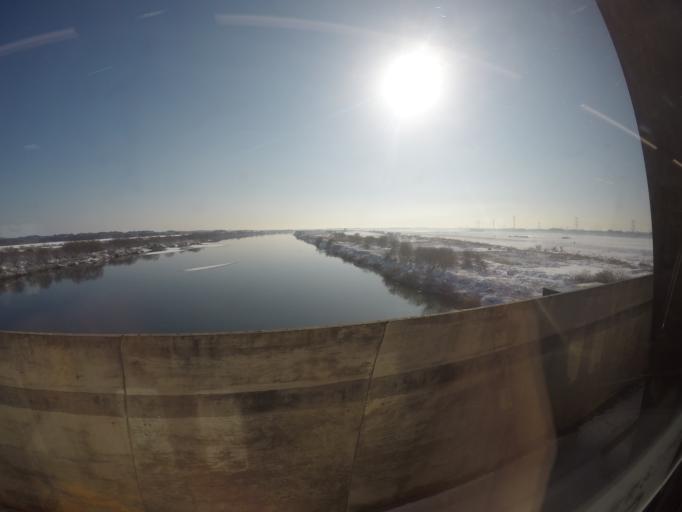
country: JP
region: Ibaraki
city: Moriya
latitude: 35.9273
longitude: 139.9638
